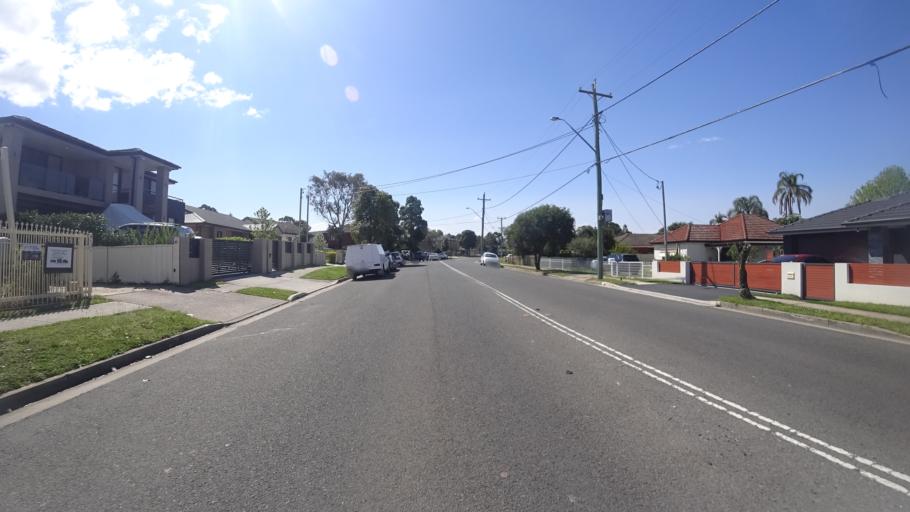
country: AU
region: New South Wales
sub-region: Fairfield
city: Cabramatta West
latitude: -33.9086
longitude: 150.9072
